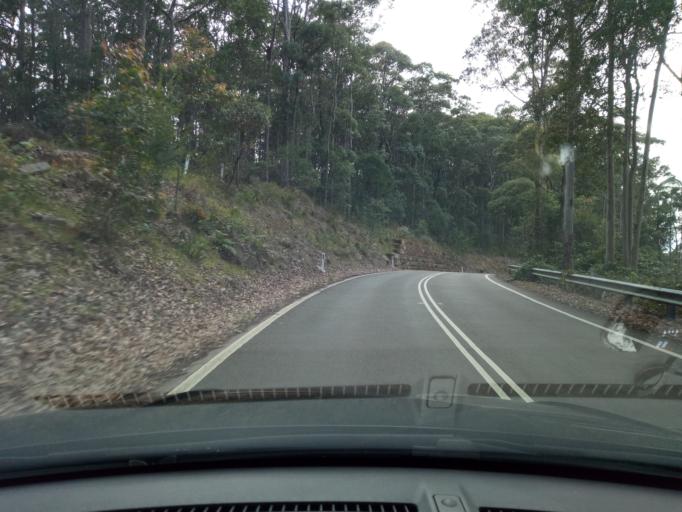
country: AU
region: New South Wales
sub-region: Gosford Shire
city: Holgate
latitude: -33.3826
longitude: 151.4280
